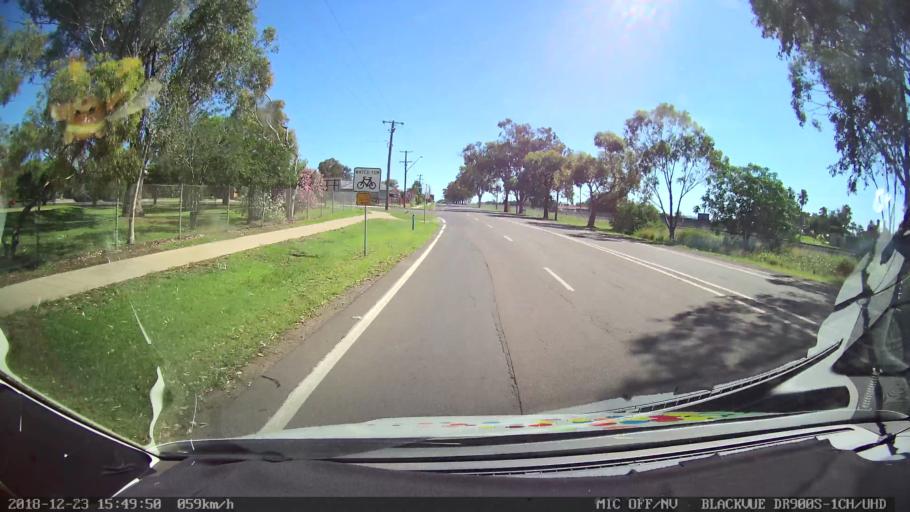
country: AU
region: New South Wales
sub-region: Tamworth Municipality
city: South Tamworth
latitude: -31.1019
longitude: 150.9041
